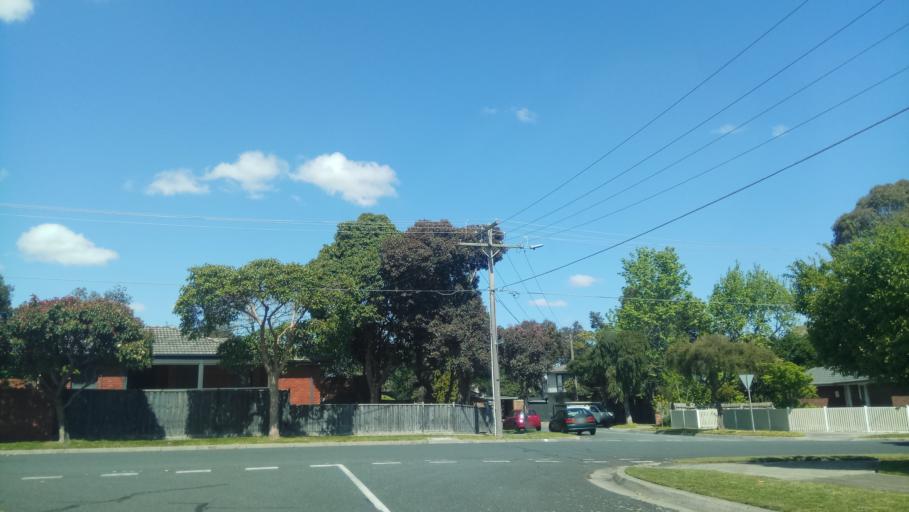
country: AU
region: Victoria
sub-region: Kingston
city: Dingley Village
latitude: -37.9821
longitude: 145.1201
